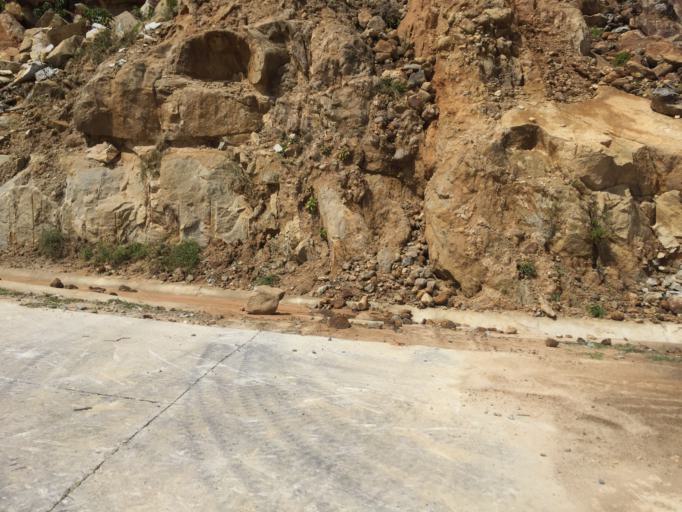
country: VN
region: Quang Nam
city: Hoi An
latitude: 15.9657
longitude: 108.5097
